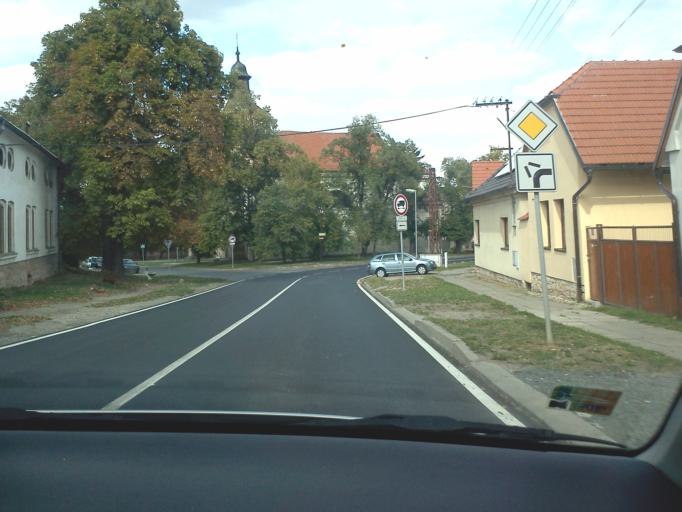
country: CZ
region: Central Bohemia
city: Cesky Brod
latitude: 50.1069
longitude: 14.8553
